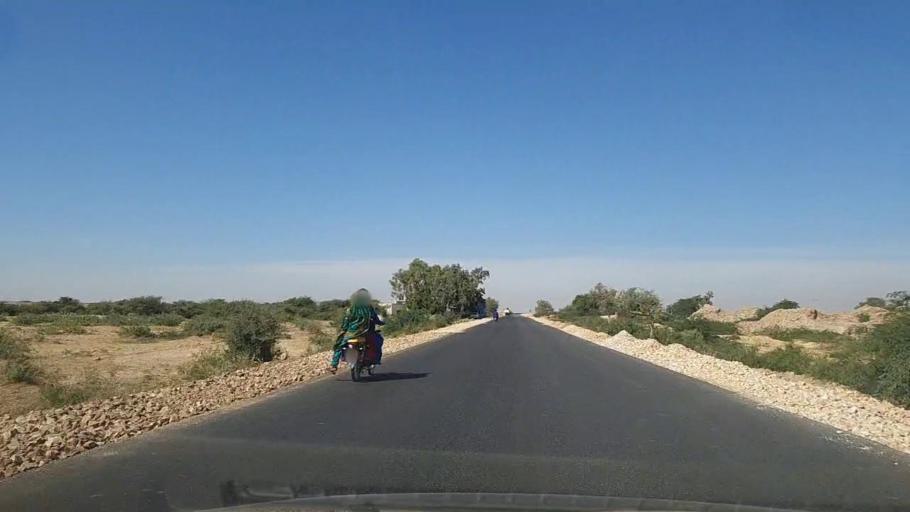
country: PK
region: Sindh
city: Kotri
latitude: 25.2918
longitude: 68.2057
